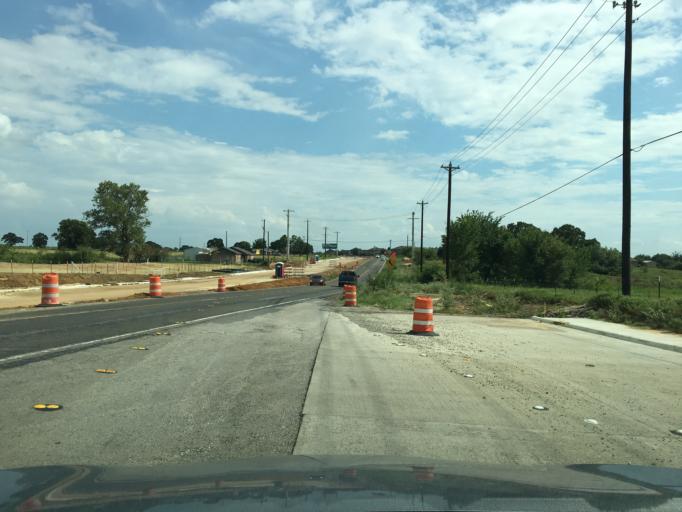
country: US
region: Texas
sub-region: Denton County
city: Cross Roads
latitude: 33.2192
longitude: -96.9767
